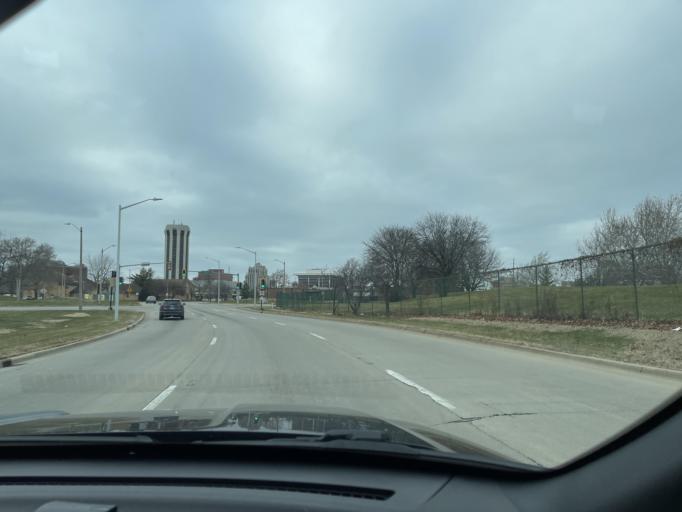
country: US
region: Illinois
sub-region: Sangamon County
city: Springfield
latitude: 39.8037
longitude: -89.6377
